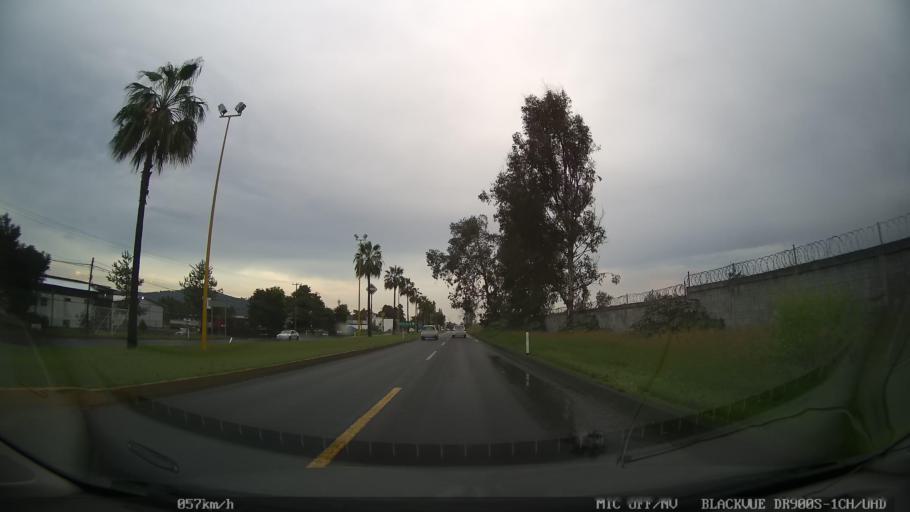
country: MX
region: Michoacan
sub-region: Uruapan
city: Santa Rosa (Santa Barbara)
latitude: 19.3864
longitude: -102.0424
